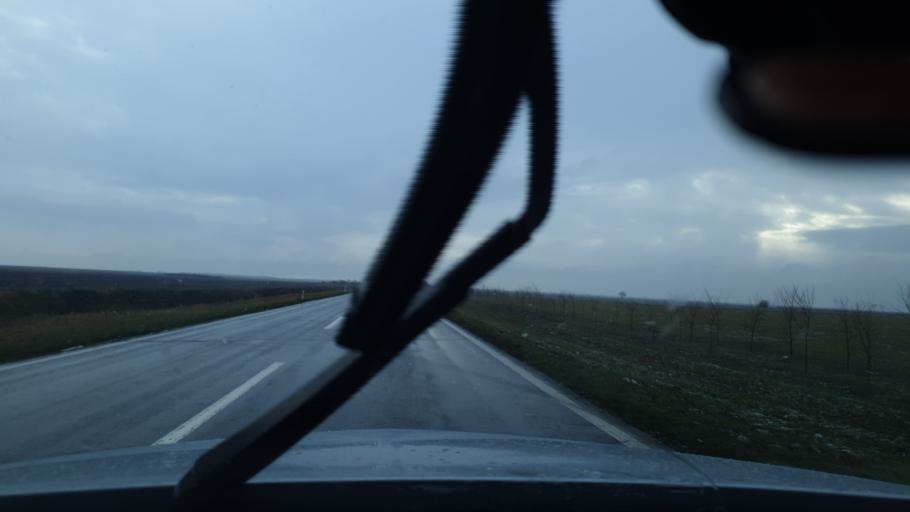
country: RS
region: Autonomna Pokrajina Vojvodina
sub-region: Juznobanatski Okrug
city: Pancevo
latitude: 44.8419
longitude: 20.7959
